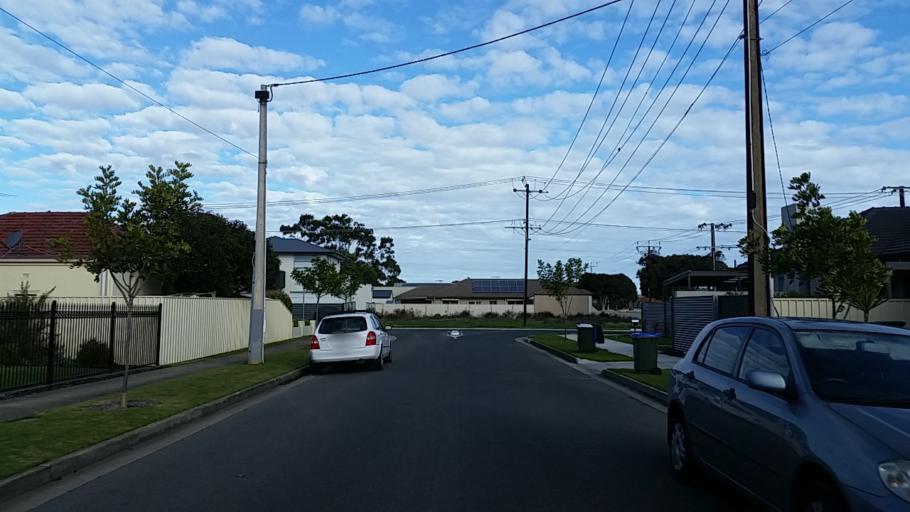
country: AU
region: South Australia
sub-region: Charles Sturt
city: Seaton
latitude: -34.8929
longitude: 138.5190
